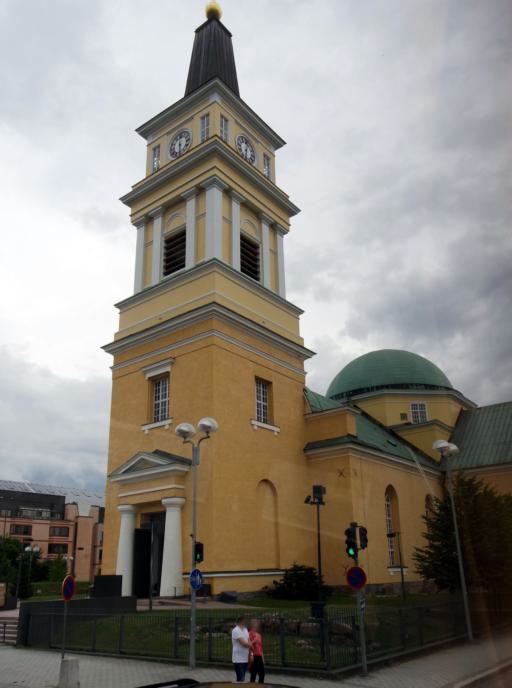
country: FI
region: Northern Ostrobothnia
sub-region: Oulu
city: Oulu
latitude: 65.0152
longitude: 25.4721
